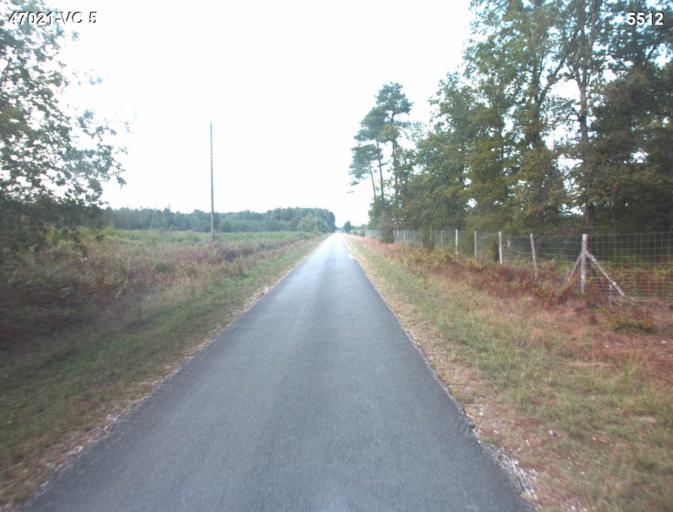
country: FR
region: Aquitaine
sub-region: Departement du Lot-et-Garonne
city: Barbaste
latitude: 44.1482
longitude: 0.2322
